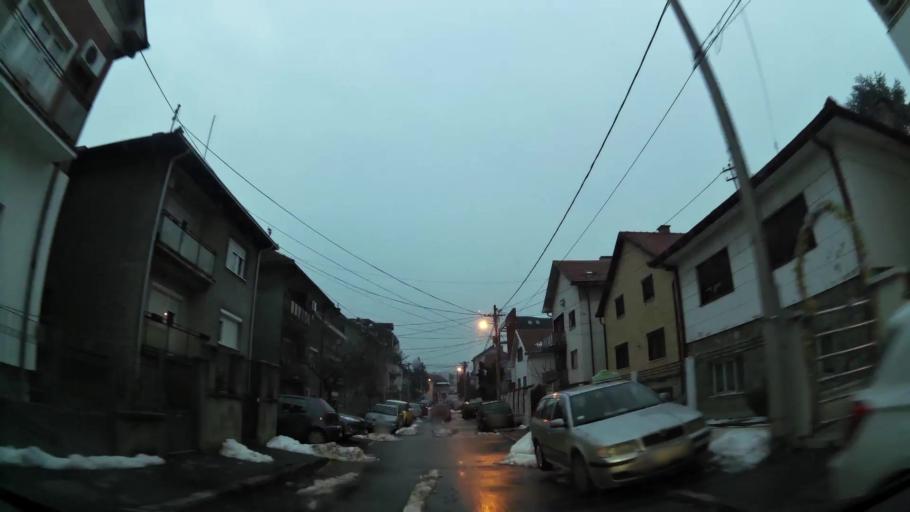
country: RS
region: Central Serbia
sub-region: Belgrade
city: Vozdovac
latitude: 44.7753
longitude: 20.4869
